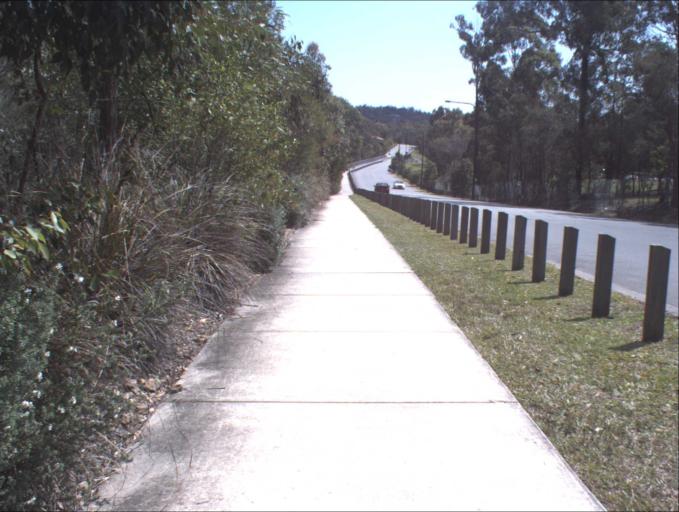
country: AU
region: Queensland
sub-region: Logan
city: Woodridge
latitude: -27.6574
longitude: 153.0788
